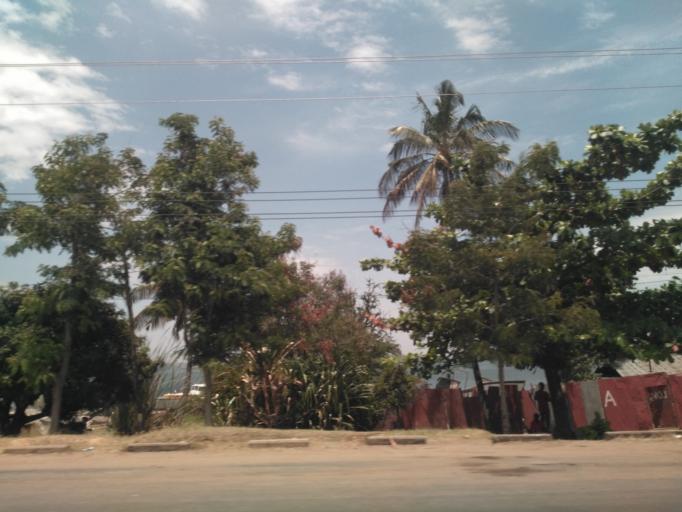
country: TZ
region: Mwanza
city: Mwanza
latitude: -2.5483
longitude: 32.9059
